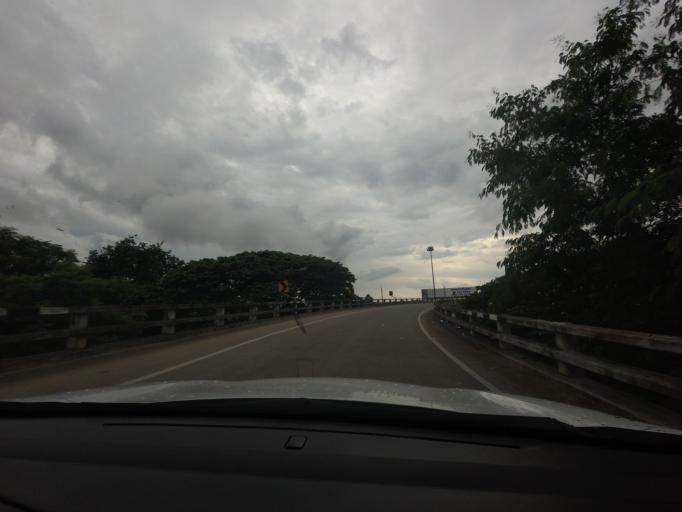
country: TH
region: Nakhon Ratchasima
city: Pak Chong
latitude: 14.6605
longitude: 101.4051
